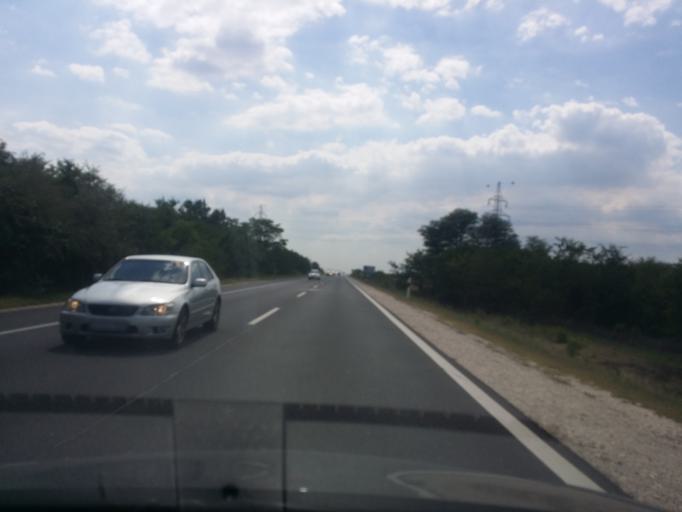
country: HU
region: Pest
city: God
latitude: 47.6657
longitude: 19.1646
